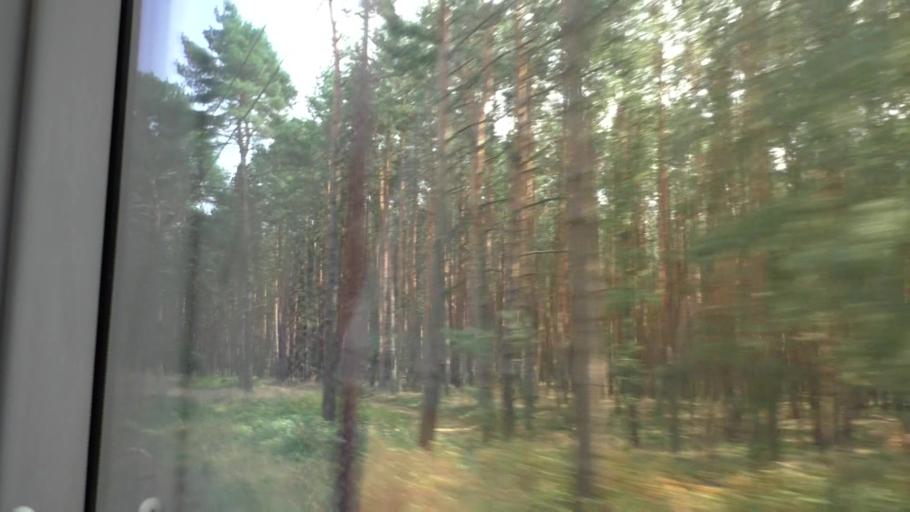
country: DE
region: Brandenburg
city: Wendisch Rietz
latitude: 52.1953
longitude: 14.0484
